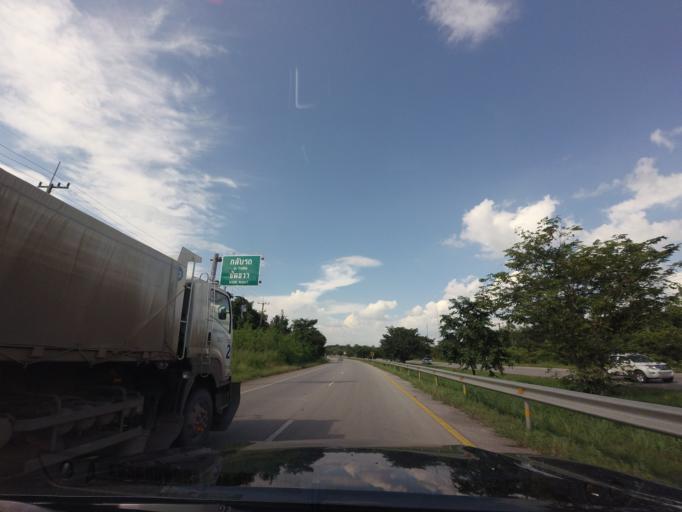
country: TH
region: Nong Khai
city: Sa Khrai
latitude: 17.6577
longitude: 102.7904
